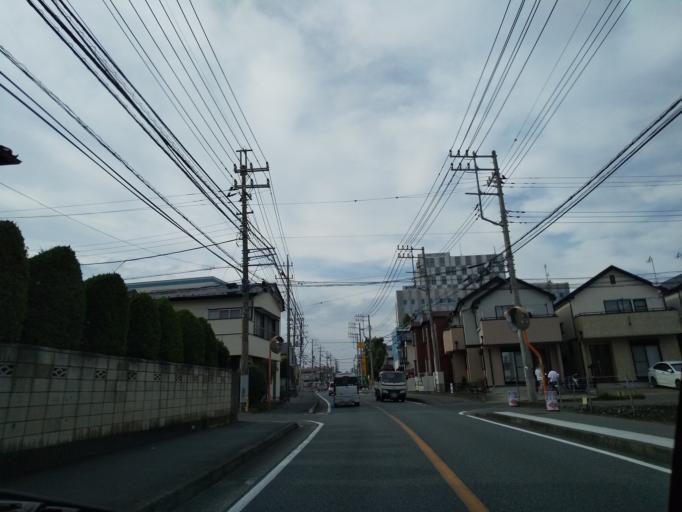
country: JP
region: Kanagawa
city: Zama
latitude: 35.4840
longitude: 139.3412
